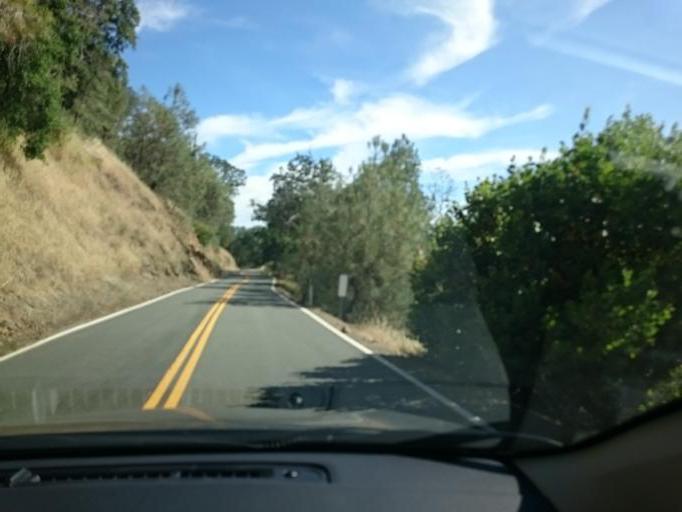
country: US
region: California
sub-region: Santa Clara County
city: East Foothills
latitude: 37.3322
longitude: -121.6670
